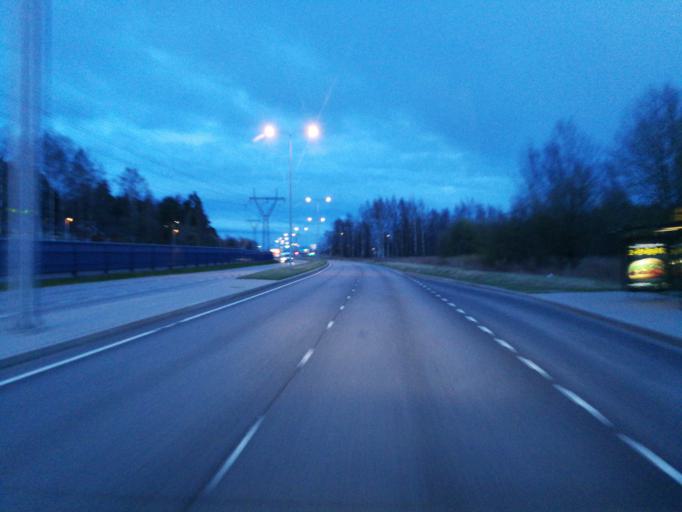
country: FI
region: Varsinais-Suomi
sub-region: Turku
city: Raisio
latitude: 60.4537
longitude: 22.1956
